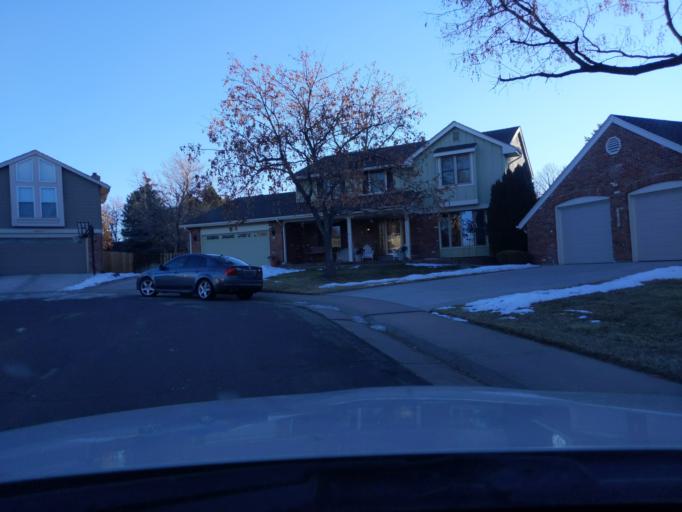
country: US
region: Colorado
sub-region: Arapahoe County
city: Centennial
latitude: 39.5718
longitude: -104.8867
